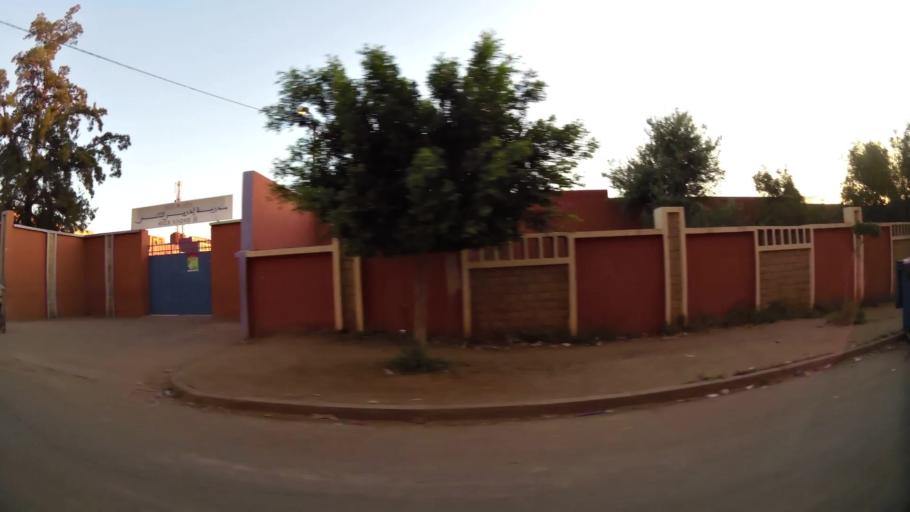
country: MA
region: Oriental
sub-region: Berkane-Taourirt
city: Berkane
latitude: 34.9176
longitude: -2.3148
